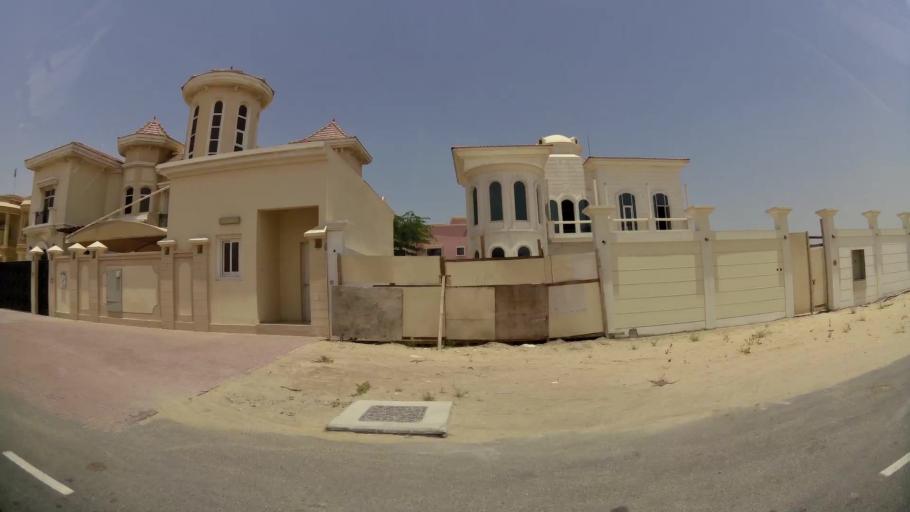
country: AE
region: Dubai
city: Dubai
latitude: 25.0897
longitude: 55.2267
